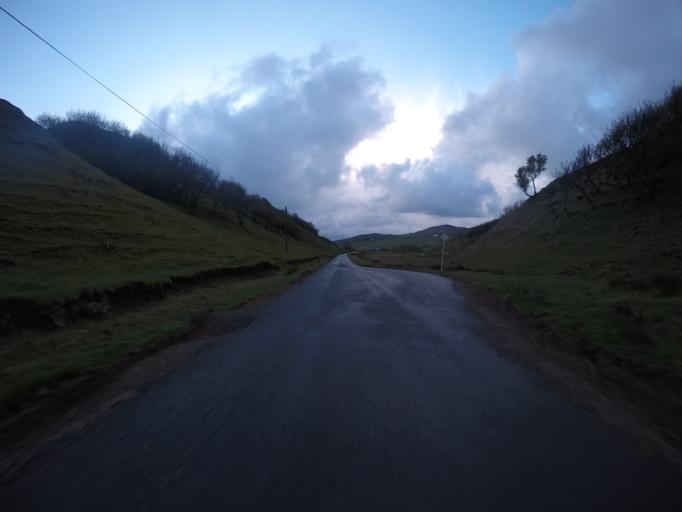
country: GB
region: Scotland
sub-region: Highland
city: Portree
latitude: 57.5838
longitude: -6.3312
